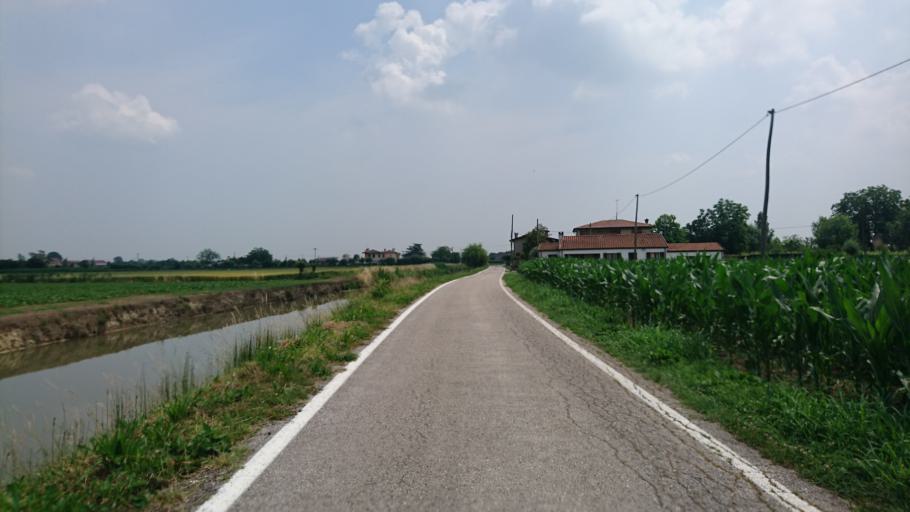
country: IT
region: Veneto
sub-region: Provincia di Padova
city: Cartura
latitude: 45.2700
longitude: 11.8744
